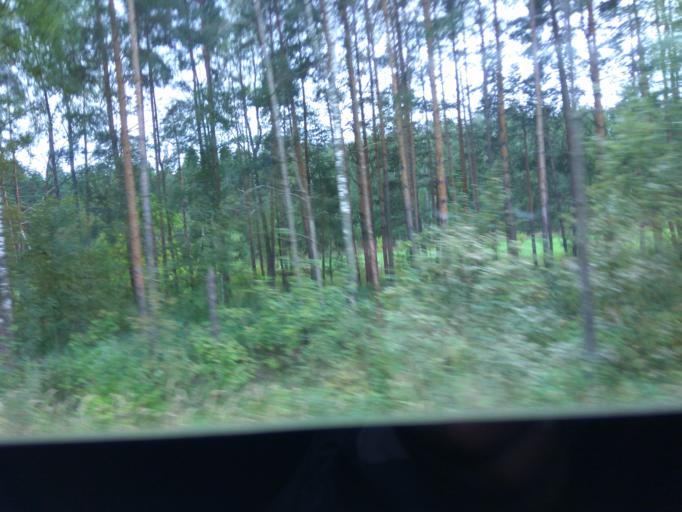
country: RU
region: Moskovskaya
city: Malyshevo
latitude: 55.5248
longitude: 38.3432
